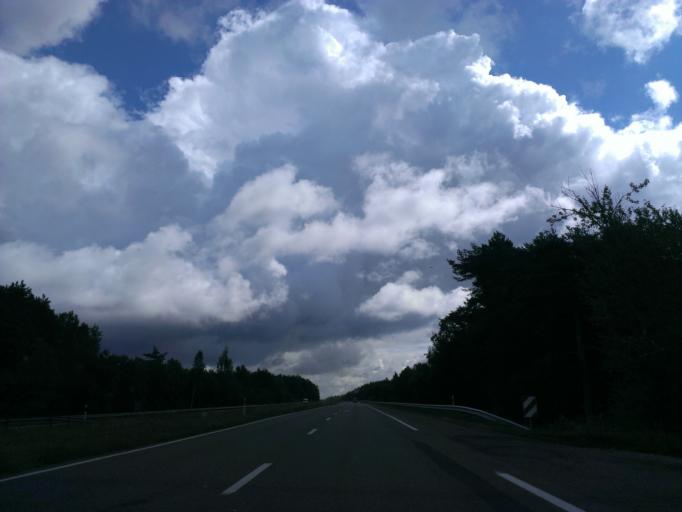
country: LV
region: Incukalns
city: Incukalns
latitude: 57.1286
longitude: 24.7167
